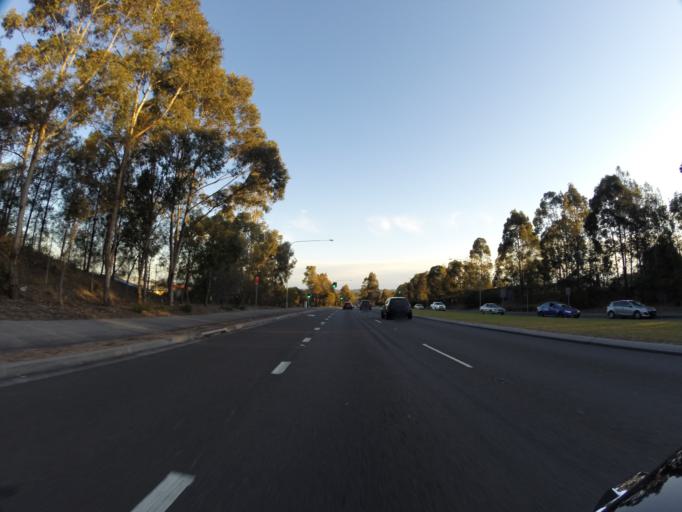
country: AU
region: New South Wales
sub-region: Fairfield
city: Cecil Park
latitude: -33.8886
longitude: 150.8613
